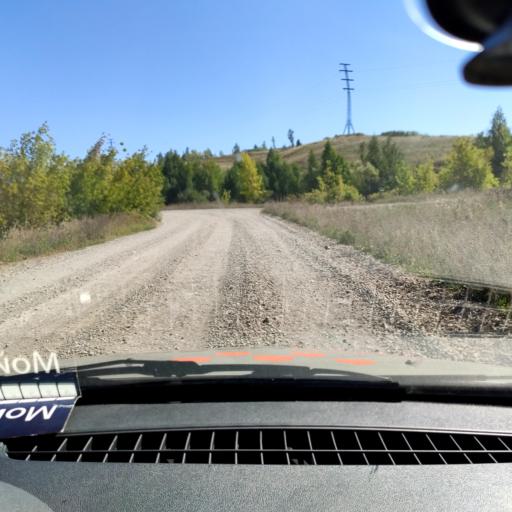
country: RU
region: Bashkortostan
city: Yermolayevo
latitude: 52.7472
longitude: 55.8331
